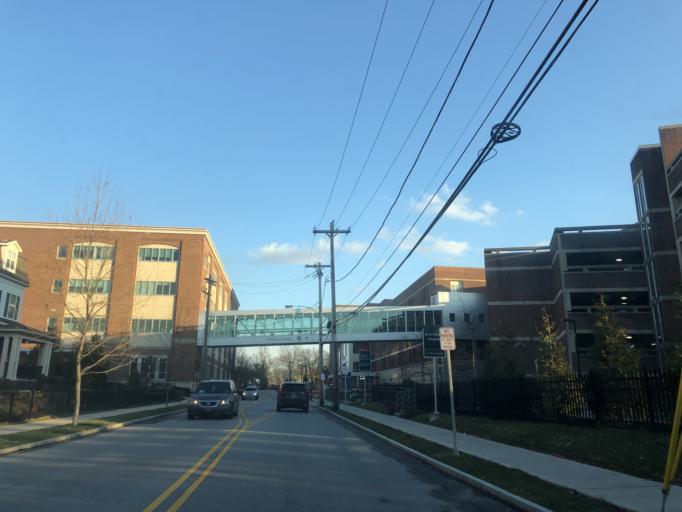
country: US
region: Pennsylvania
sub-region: Montgomery County
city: Bryn Mawr
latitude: 40.0205
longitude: -75.3227
